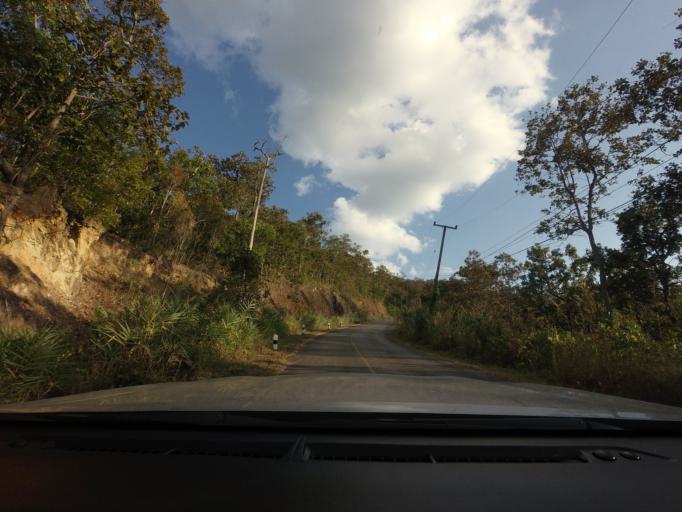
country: TH
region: Chiang Mai
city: Phrao
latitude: 19.4913
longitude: 99.1666
